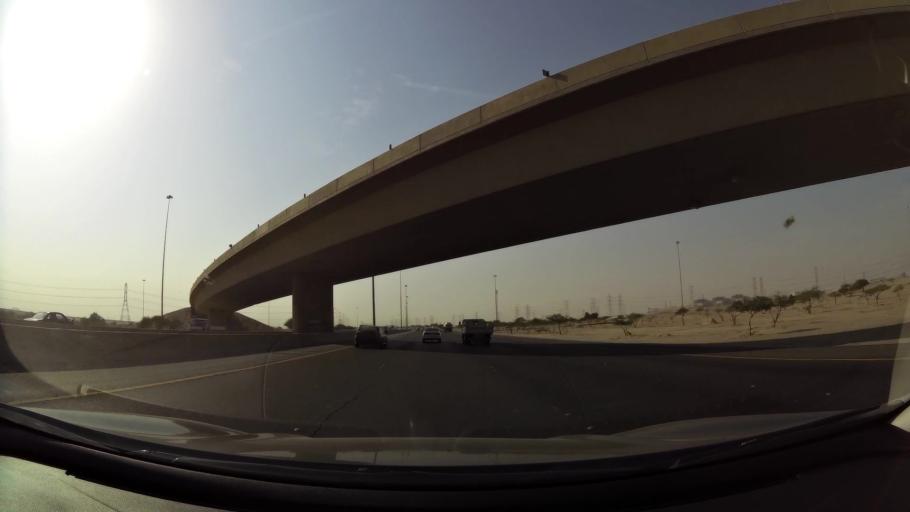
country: KW
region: Al Ahmadi
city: Al Ahmadi
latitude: 29.0312
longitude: 48.0919
